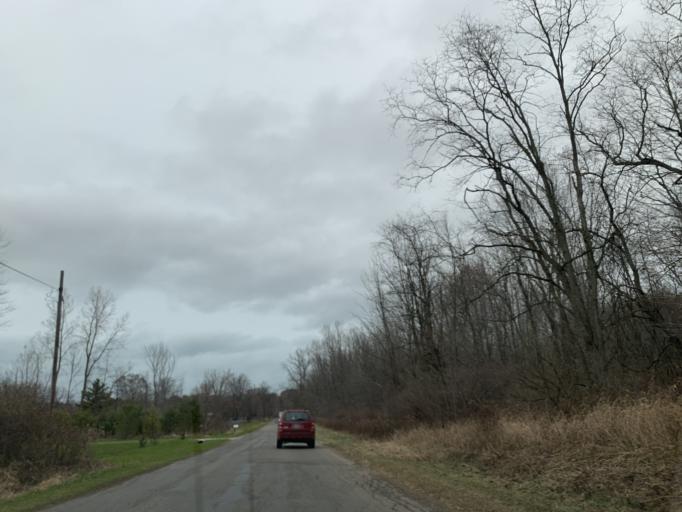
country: US
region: Michigan
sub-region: Berrien County
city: Three Oaks
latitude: 41.8100
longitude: -86.6684
